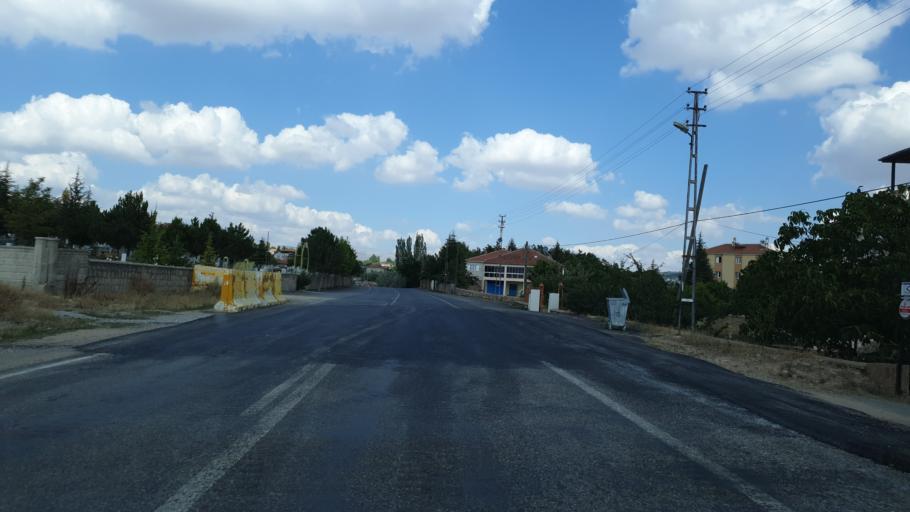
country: TR
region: Kayseri
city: Felahiye
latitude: 39.1061
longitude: 35.5979
